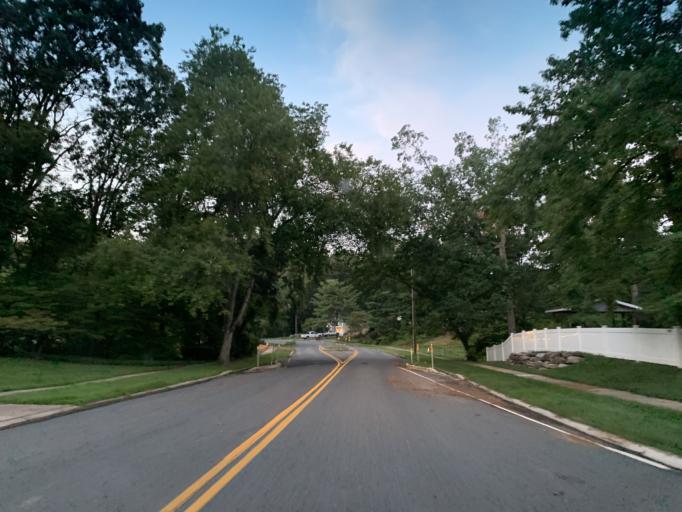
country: US
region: Maryland
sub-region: Harford County
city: Edgewood
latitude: 39.4068
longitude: -76.3424
